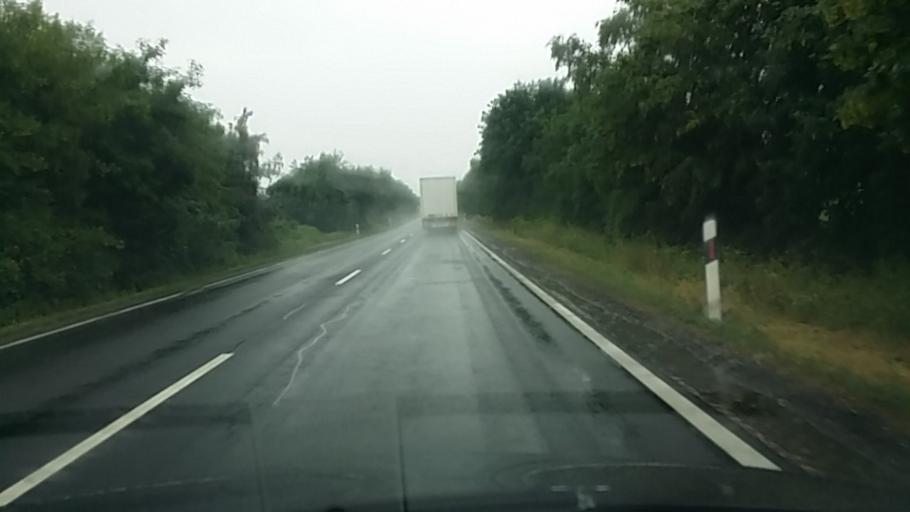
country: HU
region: Nograd
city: Retsag
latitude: 47.9665
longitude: 19.1287
